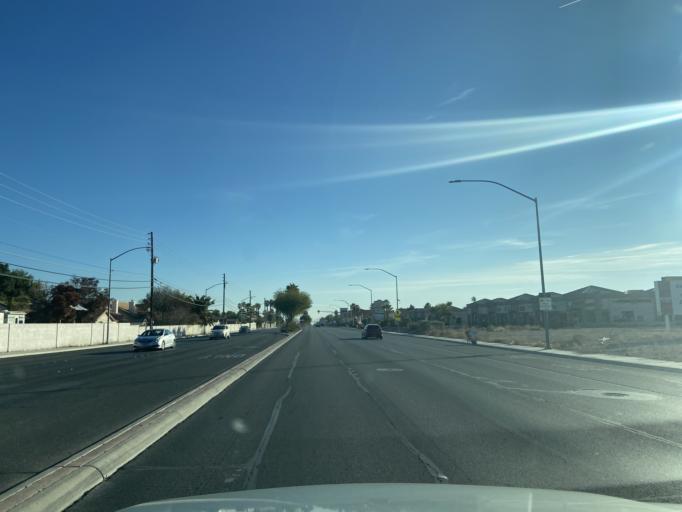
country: US
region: Nevada
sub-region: Clark County
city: North Las Vegas
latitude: 36.2392
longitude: -115.1876
